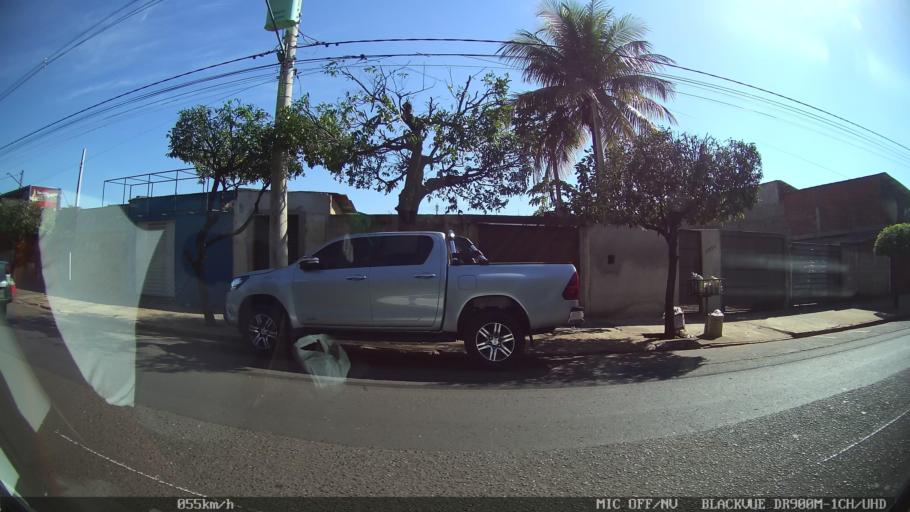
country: BR
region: Sao Paulo
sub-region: Sao Jose Do Rio Preto
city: Sao Jose do Rio Preto
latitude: -20.7961
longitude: -49.3981
